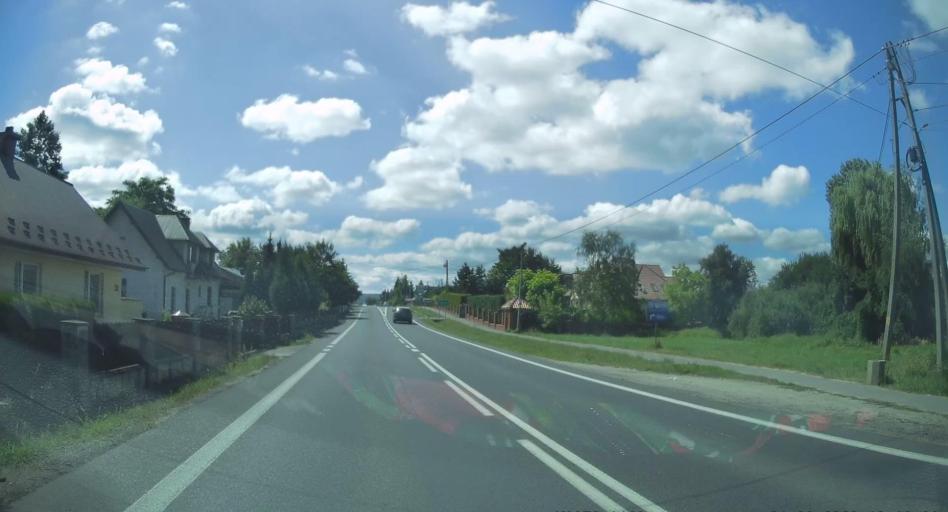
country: PL
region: Subcarpathian Voivodeship
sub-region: Powiat debicki
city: Brzeznica
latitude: 50.0747
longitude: 21.4507
